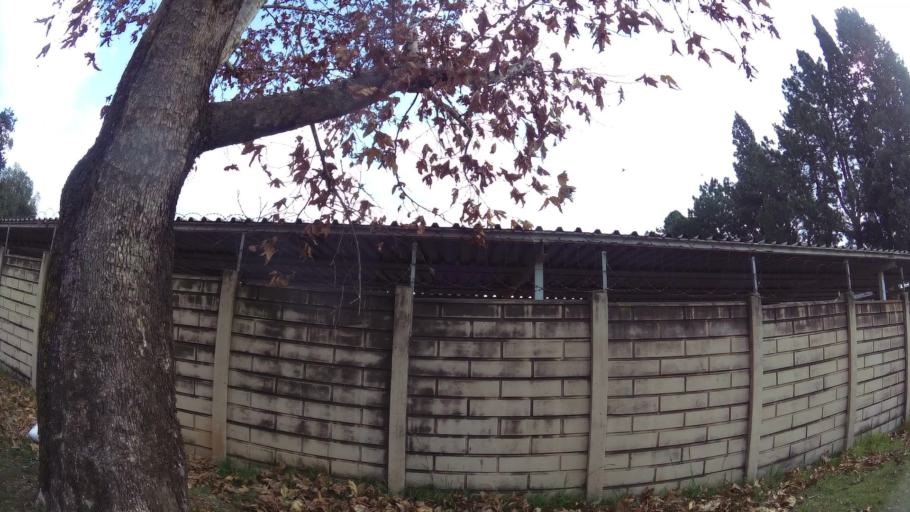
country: ZA
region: Mpumalanga
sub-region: Nkangala District Municipality
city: Delmas
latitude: -26.1471
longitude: 28.6820
